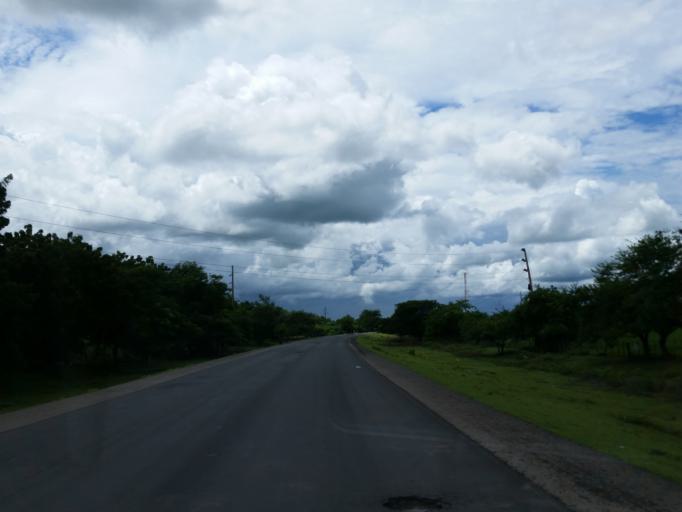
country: NI
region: Chinandega
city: Chichigalpa
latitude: 12.7871
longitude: -86.9347
